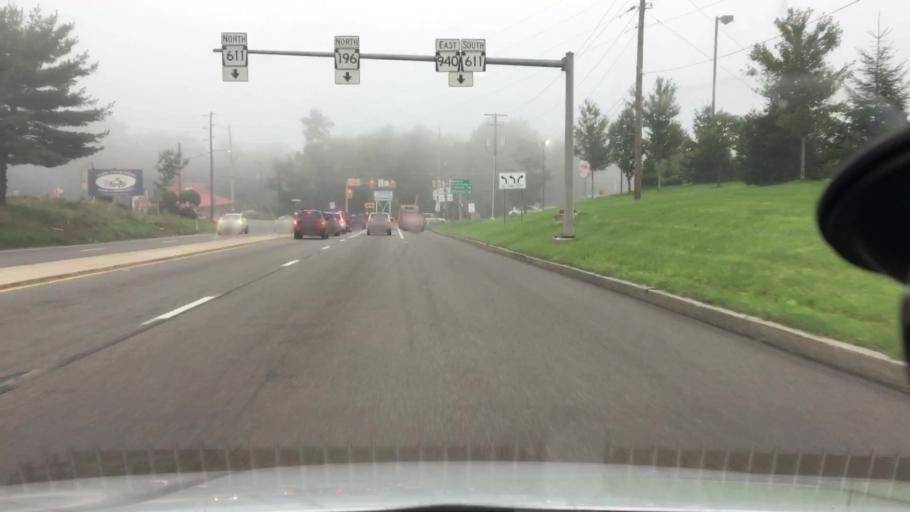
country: US
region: Pennsylvania
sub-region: Monroe County
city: Mount Pocono
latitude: 41.1261
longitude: -75.3613
